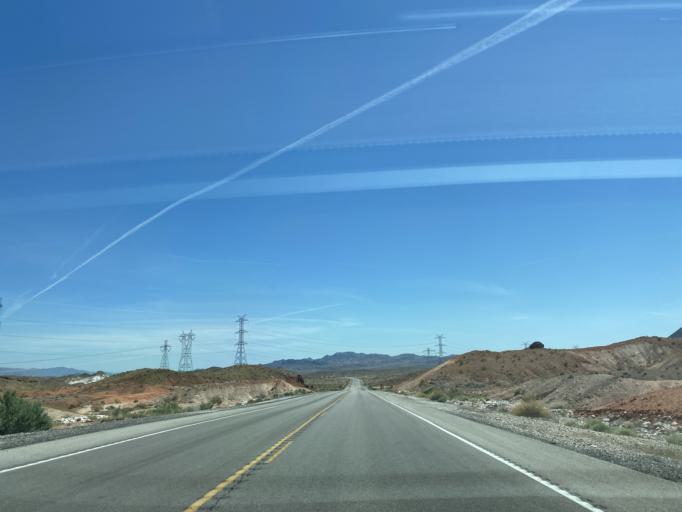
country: US
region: Nevada
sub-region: Clark County
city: Nellis Air Force Base
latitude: 36.1902
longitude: -114.9200
